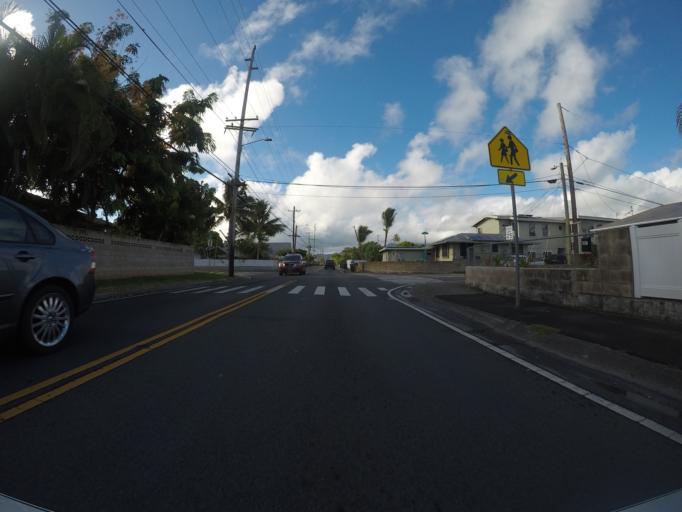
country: US
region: Hawaii
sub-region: Honolulu County
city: Kailua
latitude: 21.4033
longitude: -157.7497
